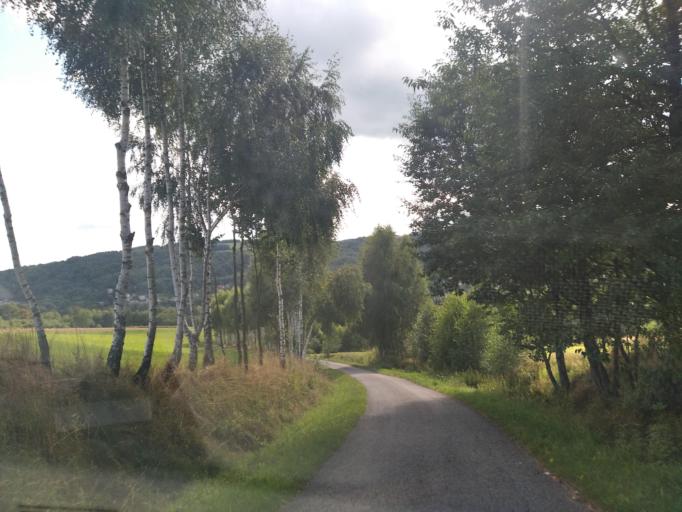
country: PL
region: Subcarpathian Voivodeship
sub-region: Powiat strzyzowski
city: Polomia
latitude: 49.8920
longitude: 21.9046
